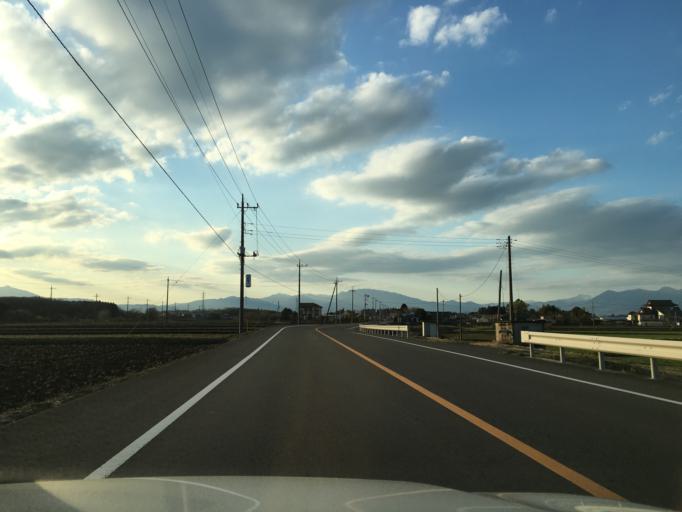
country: JP
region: Tochigi
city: Otawara
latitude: 36.8775
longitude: 140.0687
